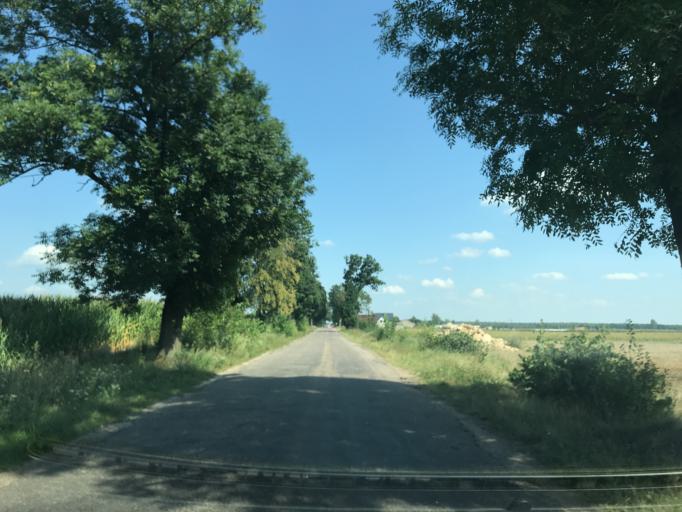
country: PL
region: Masovian Voivodeship
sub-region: Powiat zurominski
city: Lubowidz
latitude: 53.1737
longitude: 19.8850
